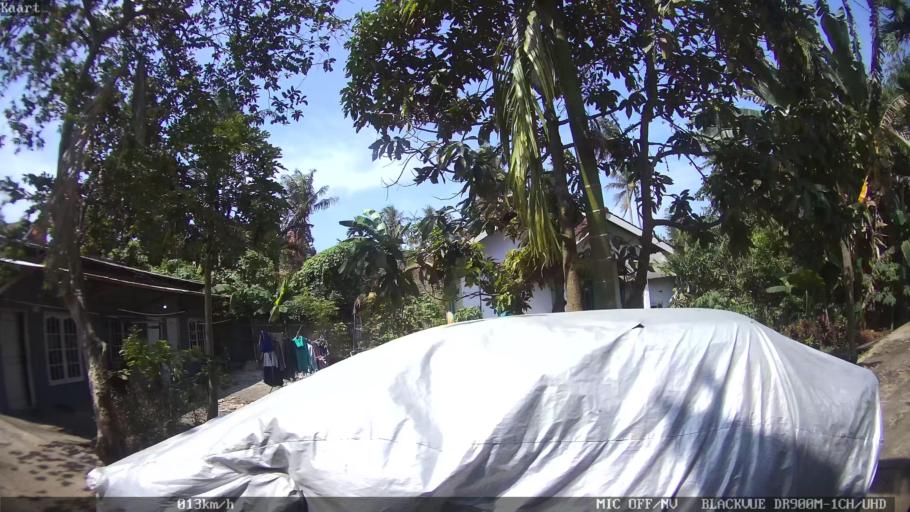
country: ID
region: Lampung
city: Kedaton
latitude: -5.3701
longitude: 105.2503
